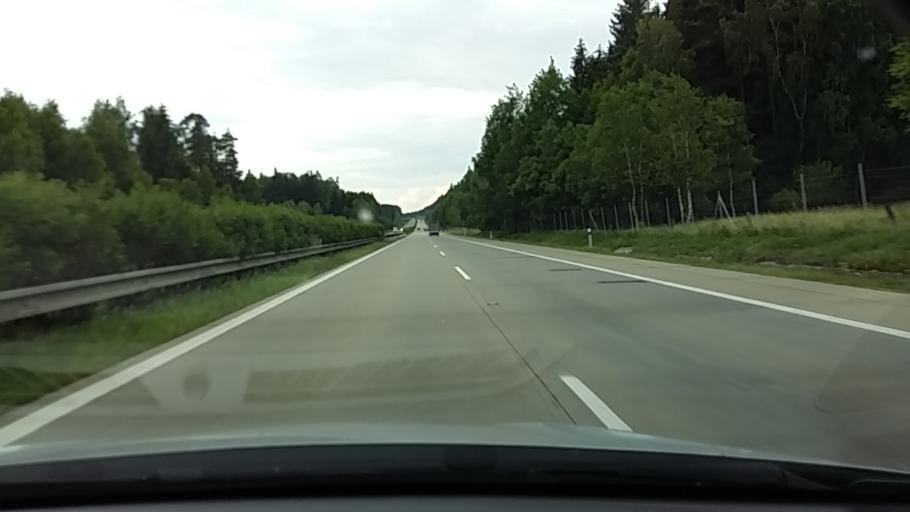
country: DE
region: Bavaria
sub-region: Upper Palatinate
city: Waidhaus
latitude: 49.6627
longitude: 12.5719
